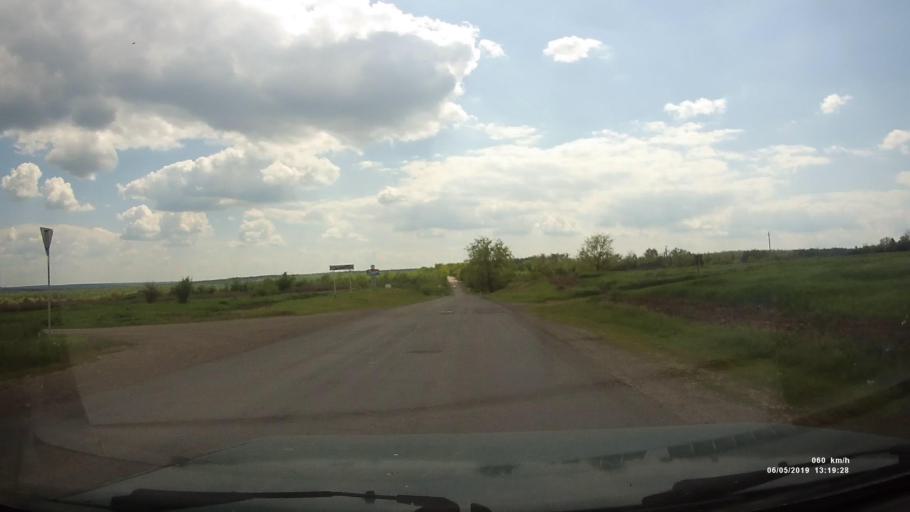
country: RU
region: Rostov
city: Ust'-Donetskiy
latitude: 47.7251
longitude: 40.9139
